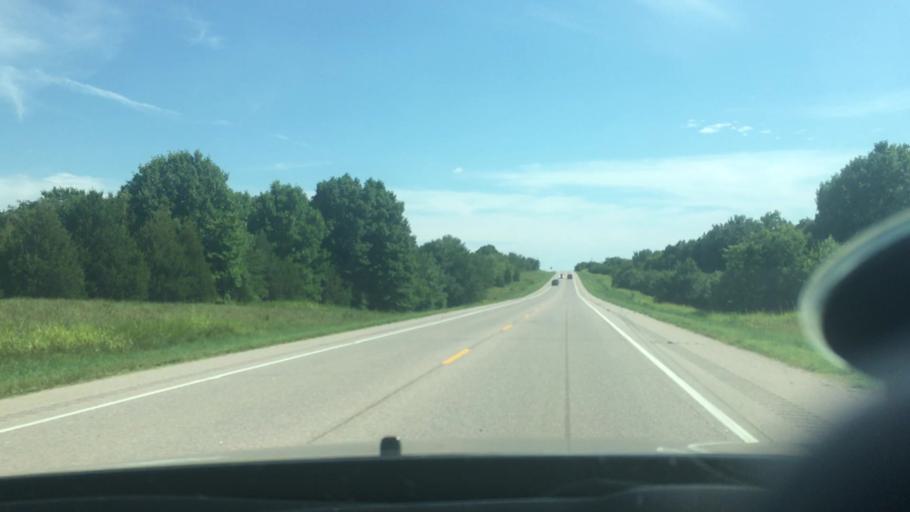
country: US
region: Oklahoma
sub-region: Seminole County
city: Konawa
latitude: 34.9925
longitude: -96.6792
